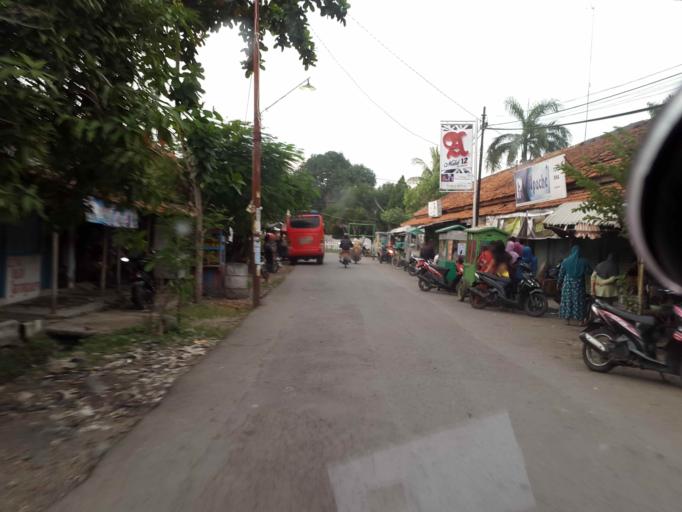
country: ID
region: Central Java
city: Comal
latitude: -6.8835
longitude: 109.5653
